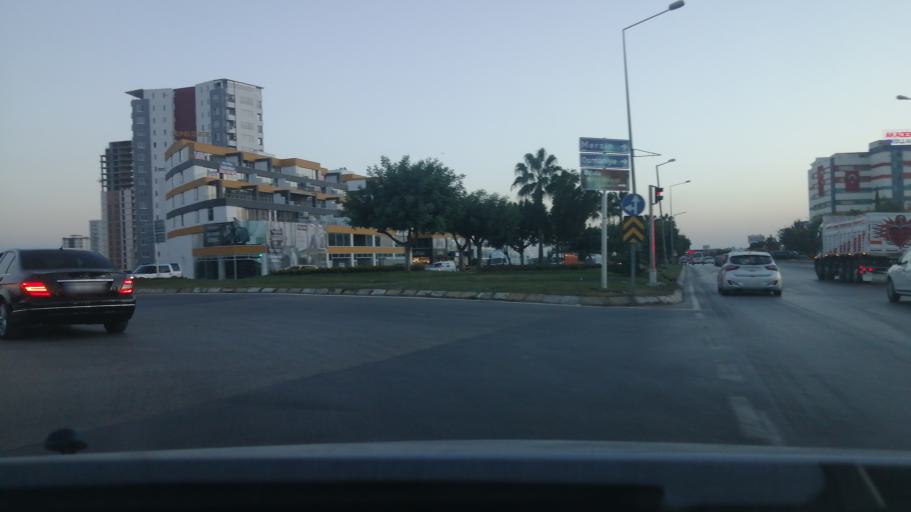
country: TR
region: Adana
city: Seyhan
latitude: 37.0154
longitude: 35.2507
